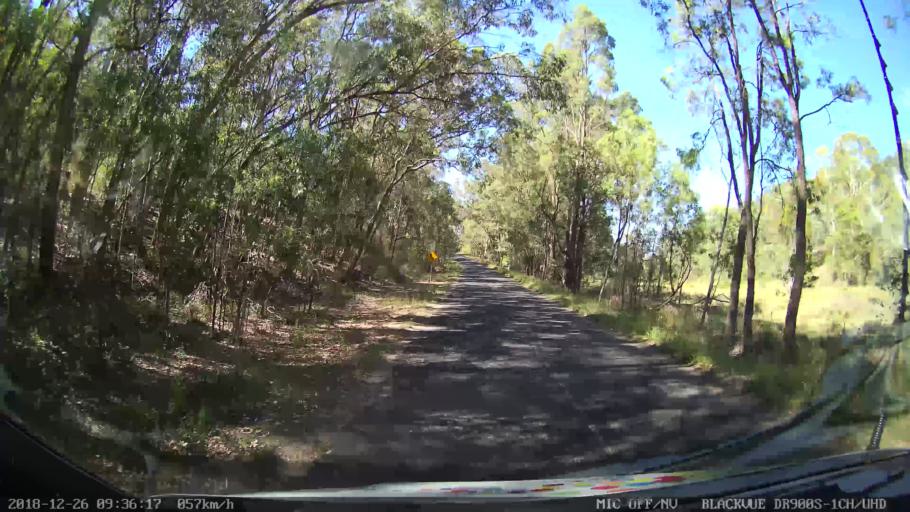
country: AU
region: New South Wales
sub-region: Mid-Western Regional
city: Kandos
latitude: -32.9225
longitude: 150.0402
